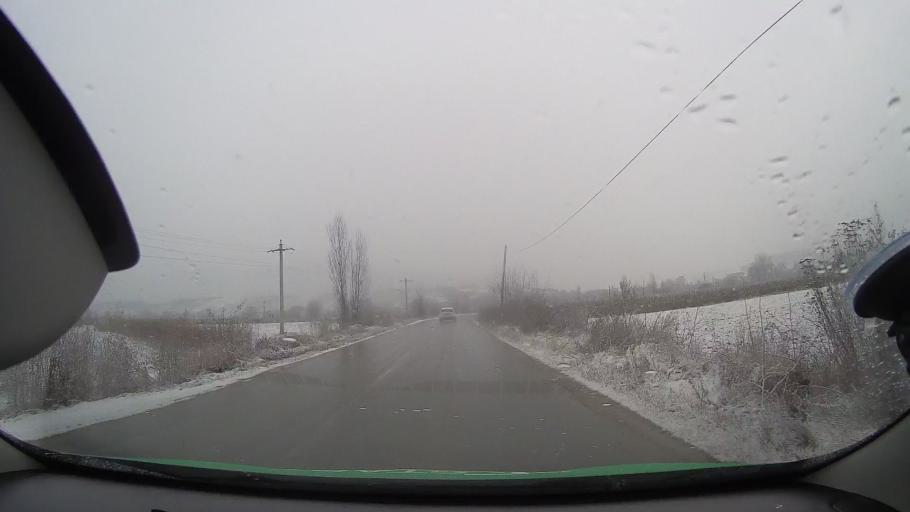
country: RO
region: Alba
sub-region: Municipiul Aiud
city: Ciumbrud
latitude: 46.3060
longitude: 23.7519
